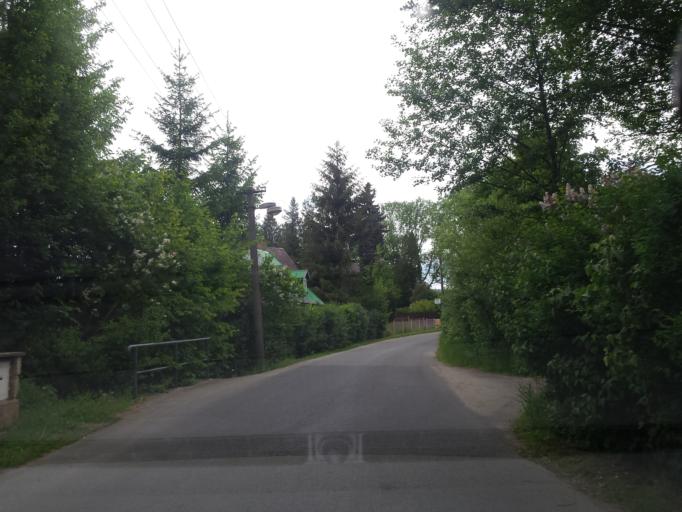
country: CZ
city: Novy Bor
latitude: 50.7448
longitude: 14.5907
